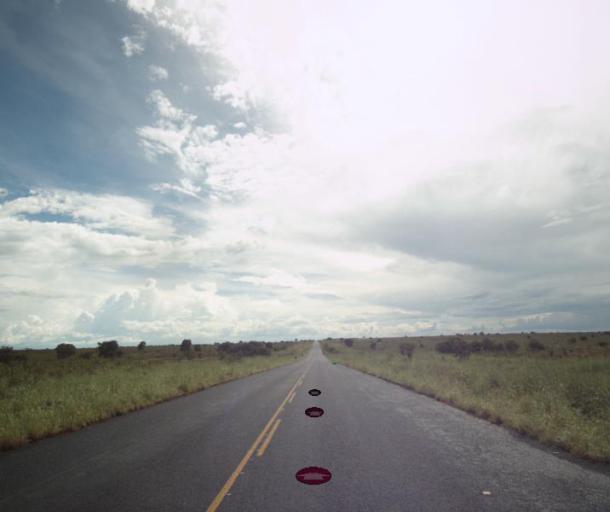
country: BR
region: Goias
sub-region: Sao Miguel Do Araguaia
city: Sao Miguel do Araguaia
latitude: -13.2960
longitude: -50.3554
